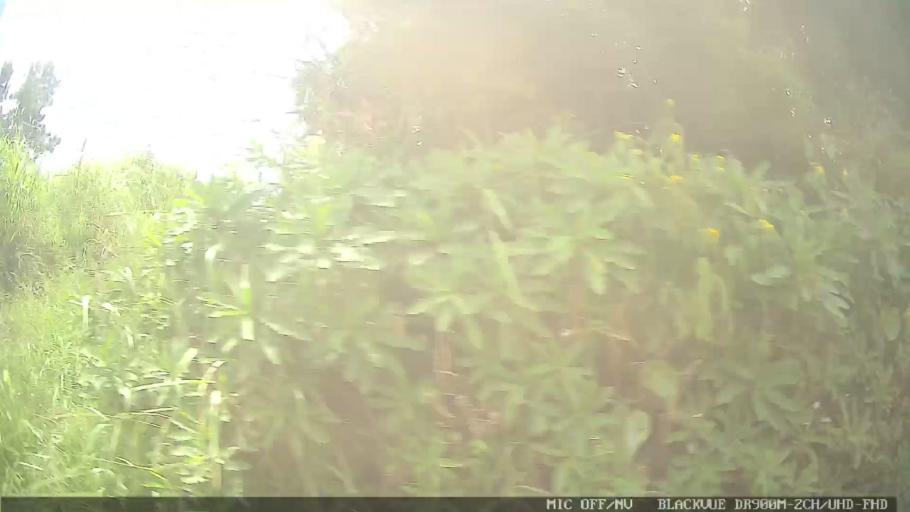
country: BR
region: Sao Paulo
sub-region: Braganca Paulista
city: Braganca Paulista
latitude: -23.0316
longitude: -46.5310
